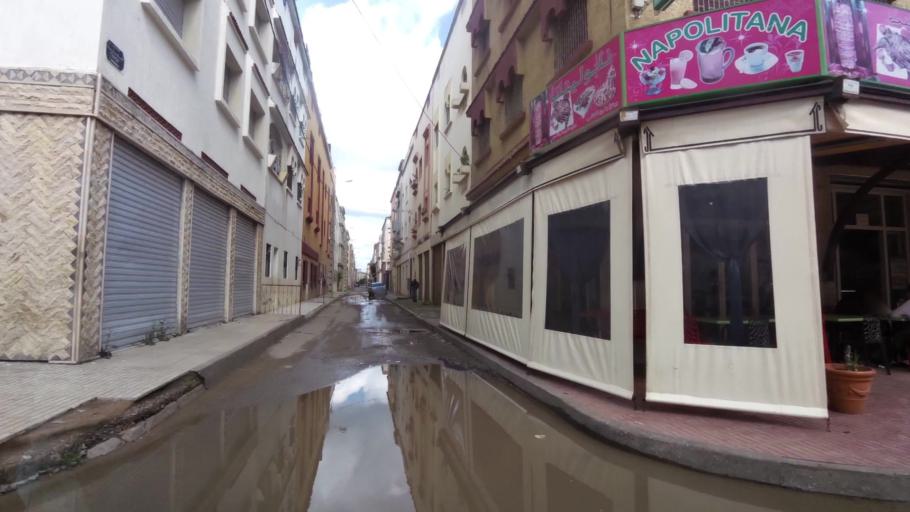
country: MA
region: Chaouia-Ouardigha
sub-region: Settat Province
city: Berrechid
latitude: 33.2656
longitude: -7.5795
